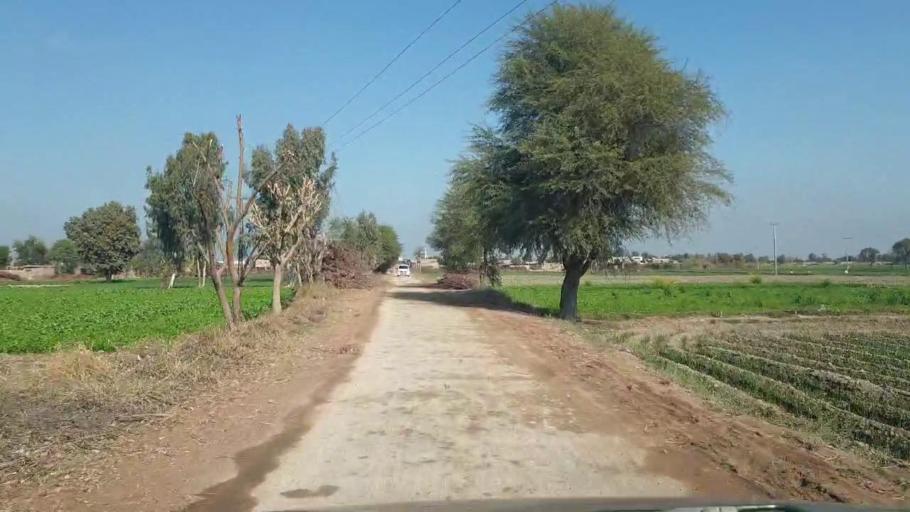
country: PK
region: Sindh
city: Bhit Shah
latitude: 25.8923
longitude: 68.5267
